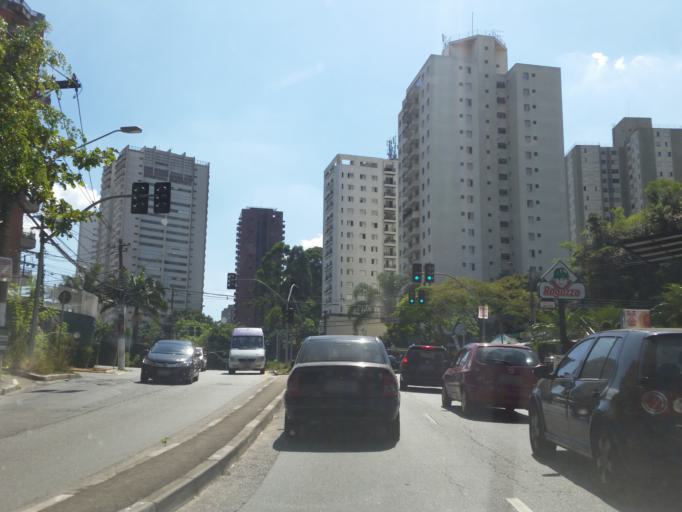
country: BR
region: Sao Paulo
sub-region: Taboao Da Serra
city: Taboao da Serra
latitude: -23.6233
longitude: -46.7377
